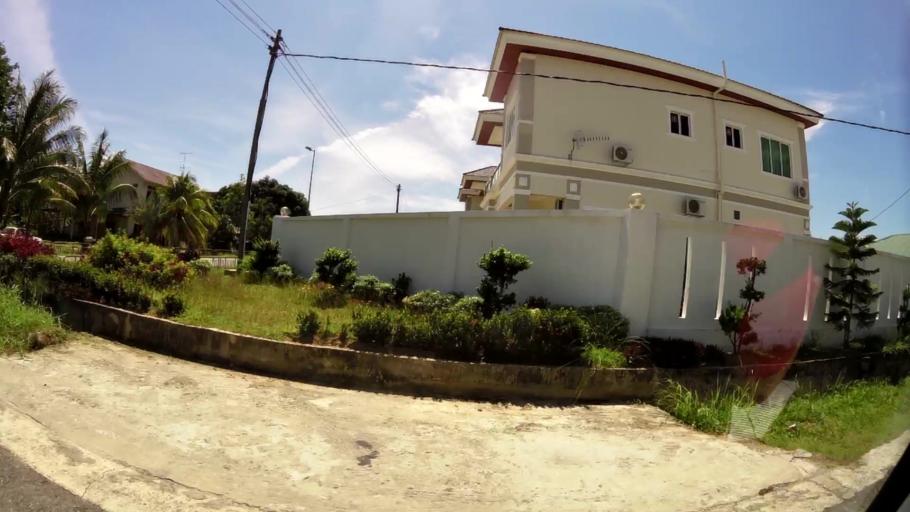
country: BN
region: Brunei and Muara
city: Bandar Seri Begawan
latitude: 4.9403
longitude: 114.9453
